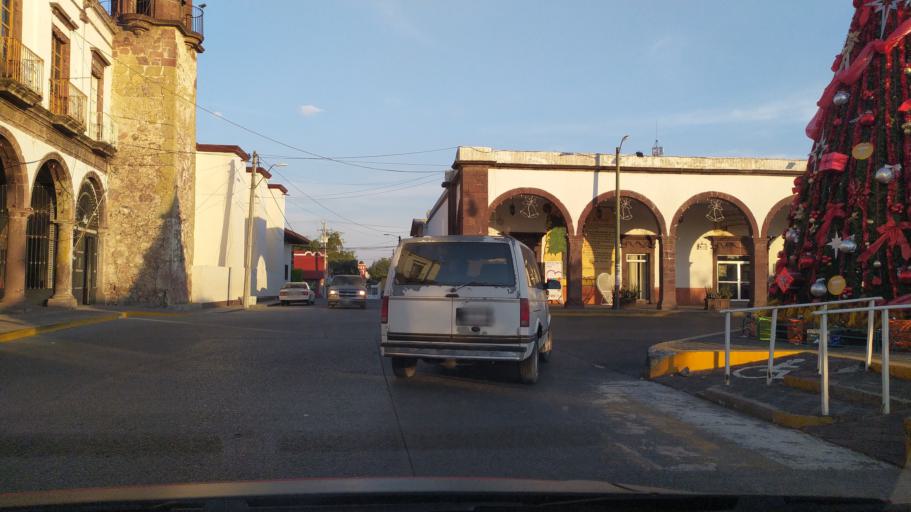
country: MX
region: Michoacan
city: Vistahermosa de Negrete
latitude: 20.2728
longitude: -102.4738
